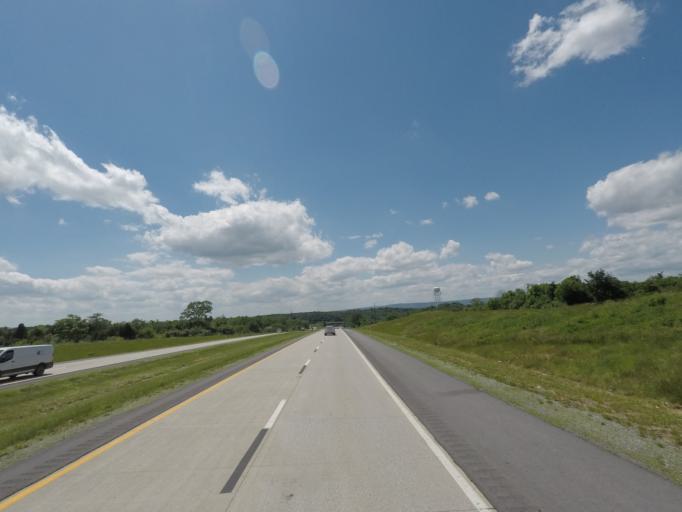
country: US
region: West Virginia
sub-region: Berkeley County
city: Martinsburg
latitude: 39.3939
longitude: -77.9080
